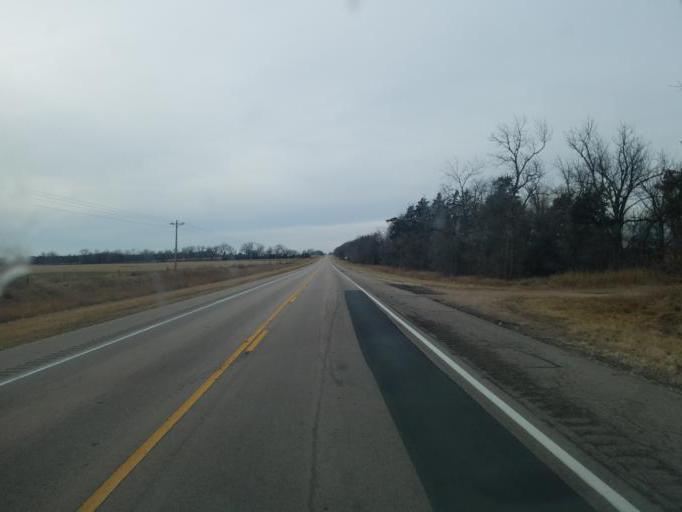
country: US
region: Nebraska
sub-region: Antelope County
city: Neligh
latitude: 42.3352
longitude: -98.1362
